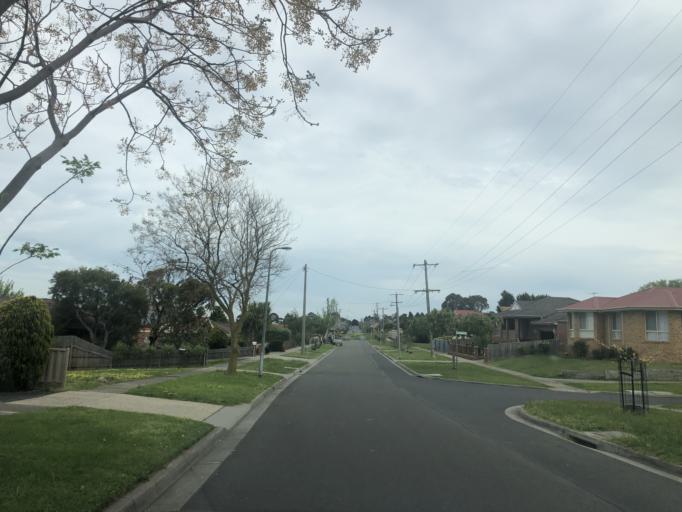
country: AU
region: Victoria
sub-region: Casey
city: Hallam
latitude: -38.0027
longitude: 145.2803
